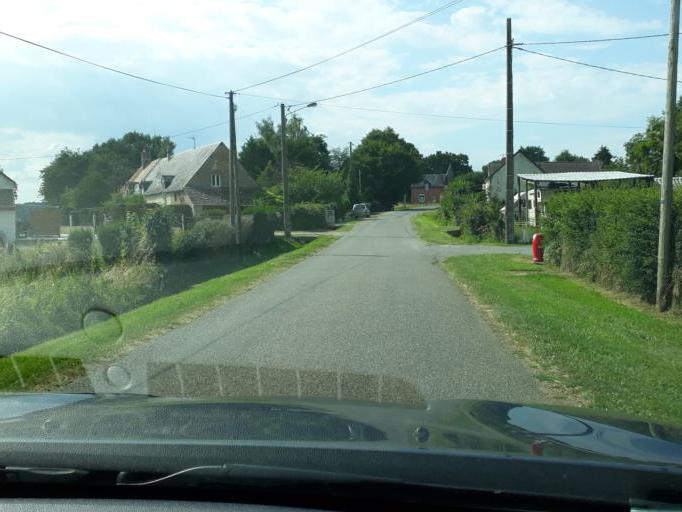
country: FR
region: Centre
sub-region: Departement du Cher
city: Jouet-sur-l'Aubois
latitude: 47.0121
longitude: 2.9102
